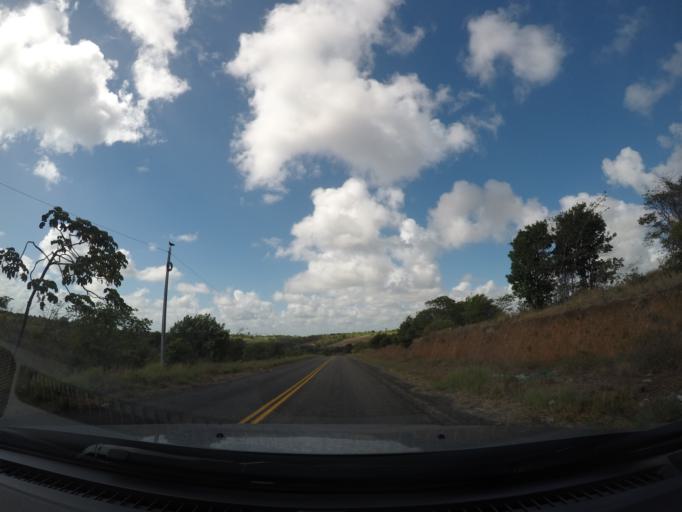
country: BR
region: Paraiba
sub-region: Pitimbu
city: Pitimbu
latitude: -7.4157
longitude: -34.8266
